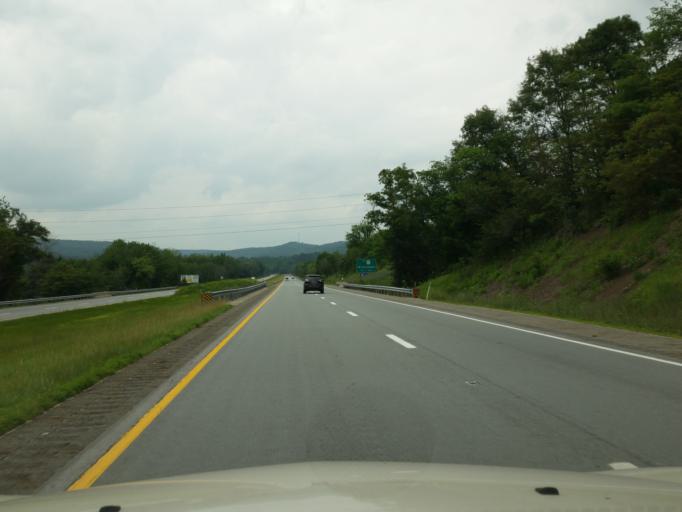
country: US
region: Pennsylvania
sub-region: Perry County
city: Newport
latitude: 40.5278
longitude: -77.1350
